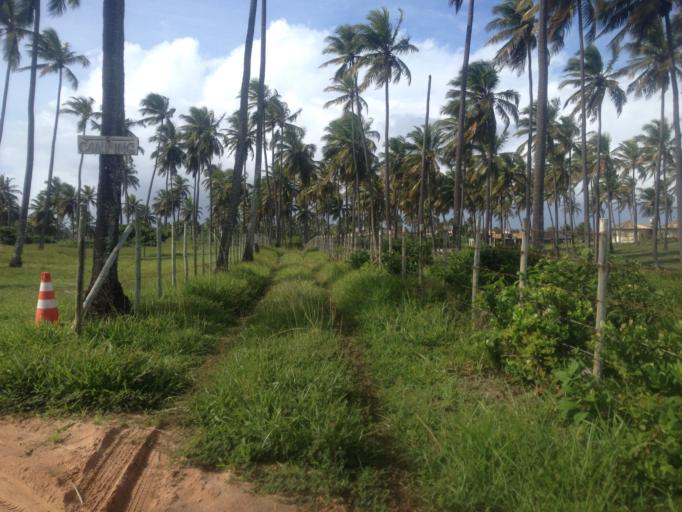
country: BR
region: Bahia
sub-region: Mata De Sao Joao
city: Mata de Sao Joao
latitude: -12.5000
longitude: -37.9617
